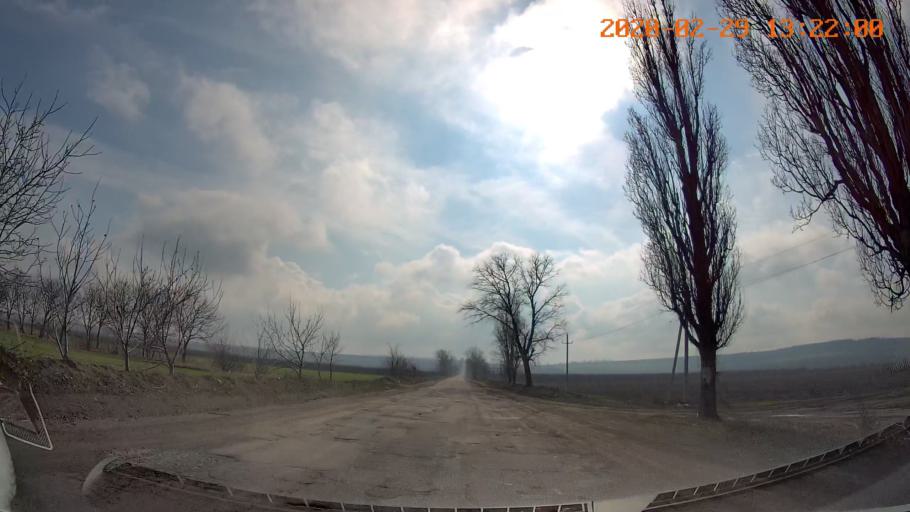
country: MD
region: Telenesti
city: Camenca
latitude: 47.9653
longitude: 28.6287
